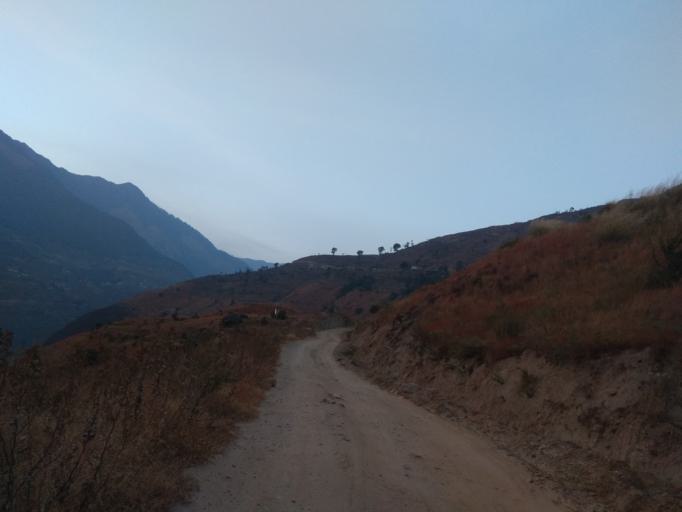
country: NP
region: Far Western
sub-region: Seti Zone
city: Achham
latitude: 29.2250
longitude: 81.6337
